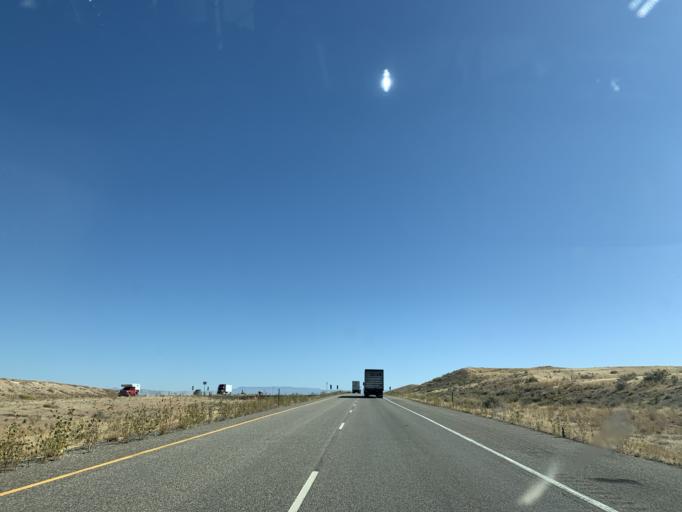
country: US
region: Colorado
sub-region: Mesa County
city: Loma
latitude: 39.2184
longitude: -108.8791
